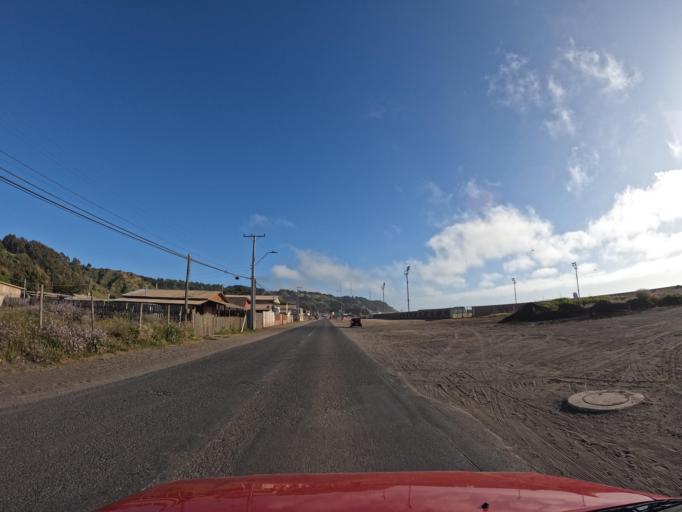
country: CL
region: Maule
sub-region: Provincia de Talca
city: Constitucion
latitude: -34.9306
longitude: -72.1801
